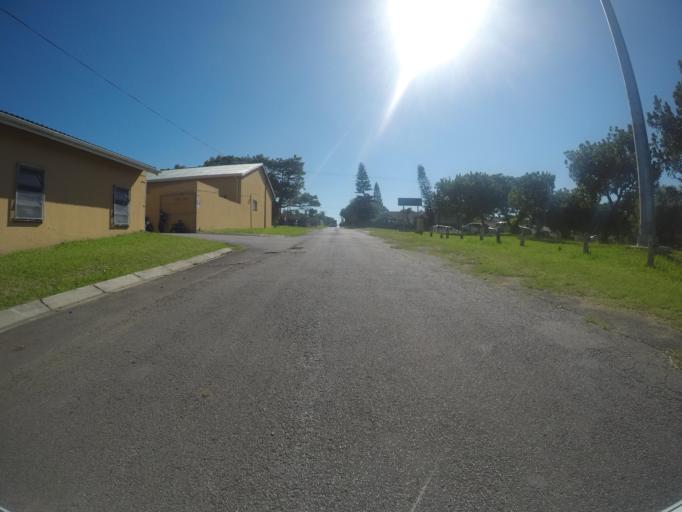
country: ZA
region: Eastern Cape
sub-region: Buffalo City Metropolitan Municipality
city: East London
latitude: -32.9407
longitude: 28.0031
